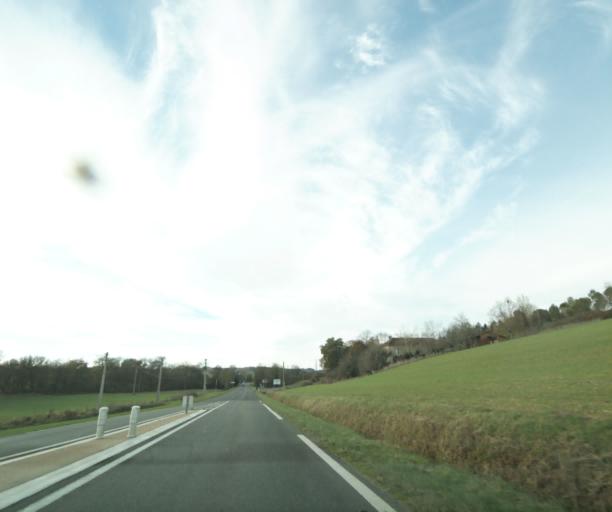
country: FR
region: Midi-Pyrenees
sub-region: Departement du Gers
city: Jegun
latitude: 43.6932
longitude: 0.4645
